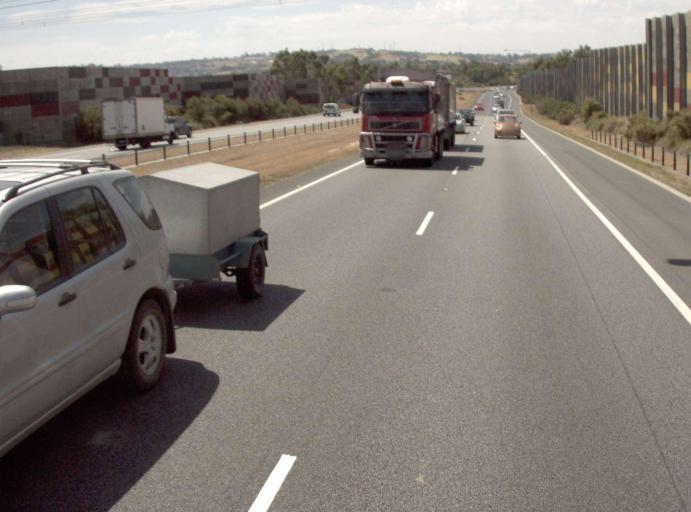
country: AU
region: Victoria
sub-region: Casey
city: Hallam
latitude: -37.9991
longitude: 145.2844
